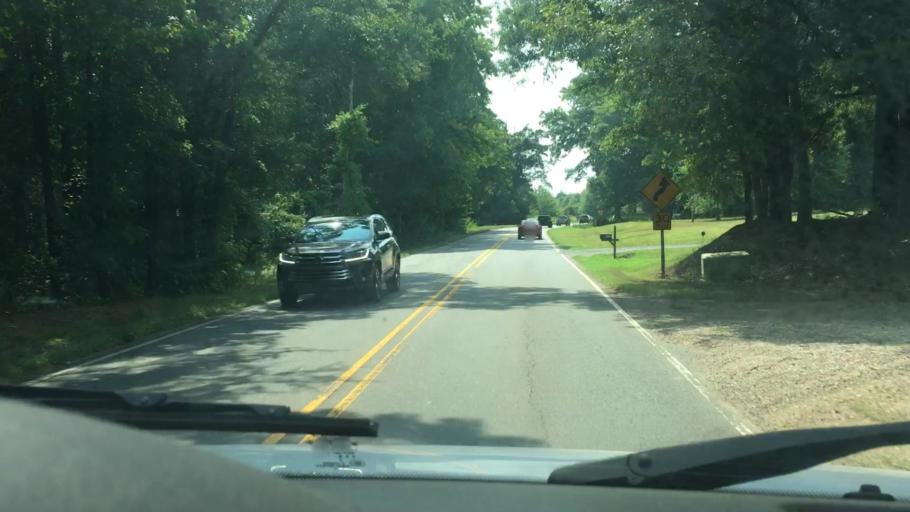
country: US
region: North Carolina
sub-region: Mecklenburg County
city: Huntersville
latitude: 35.4067
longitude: -80.8983
